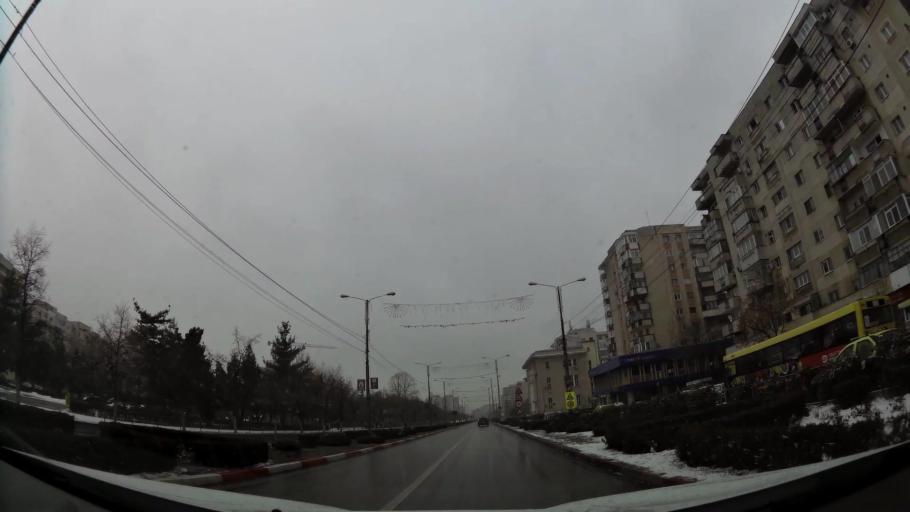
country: RO
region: Prahova
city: Ploiesti
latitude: 44.9469
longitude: 26.0113
